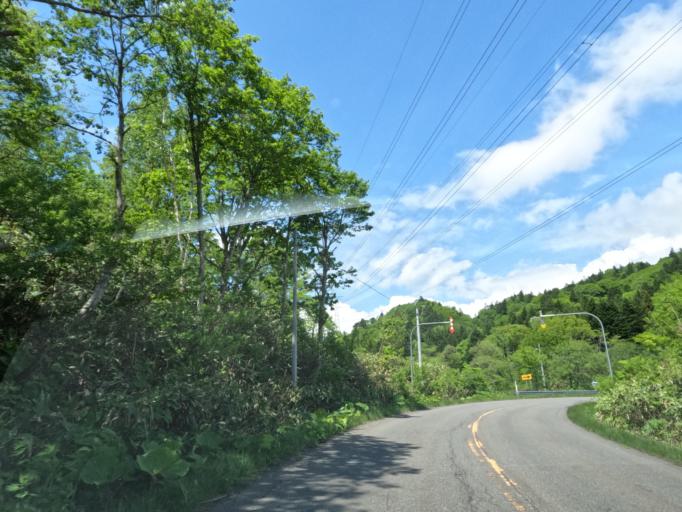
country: JP
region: Hokkaido
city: Takikawa
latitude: 43.5485
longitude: 141.6166
